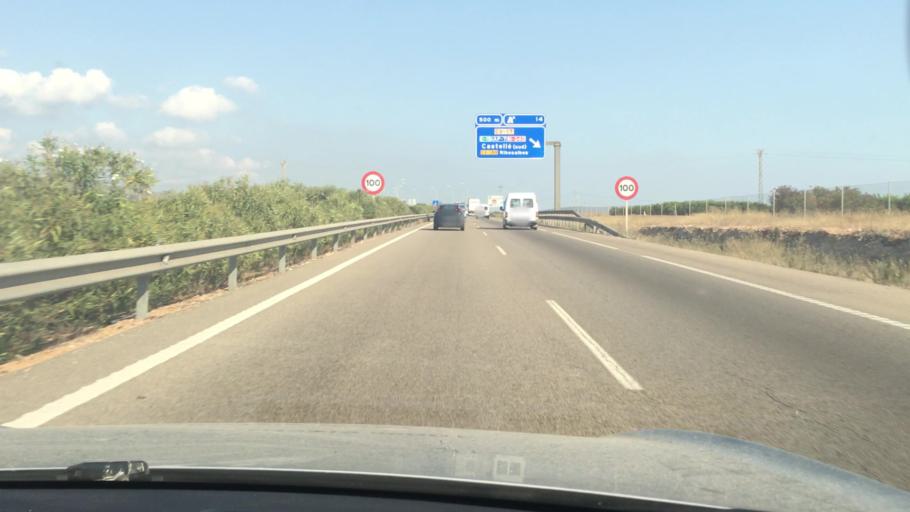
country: ES
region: Valencia
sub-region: Provincia de Castello
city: Vila-real
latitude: 39.9841
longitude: -0.1302
